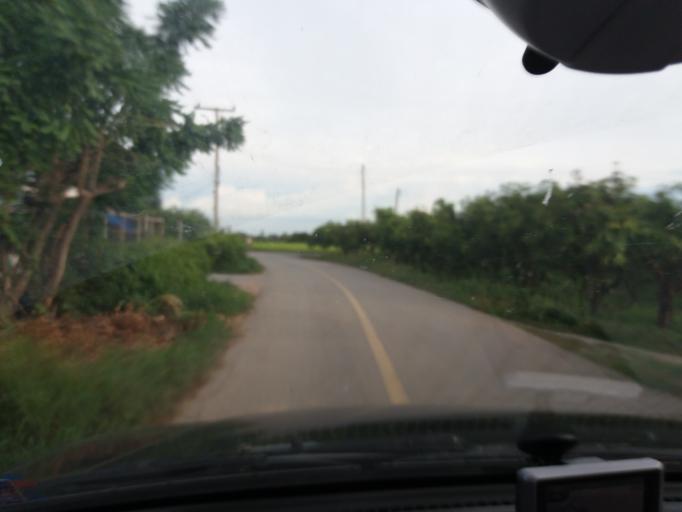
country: TH
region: Suphan Buri
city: Doembang Nangbuat
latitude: 14.8126
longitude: 100.1394
